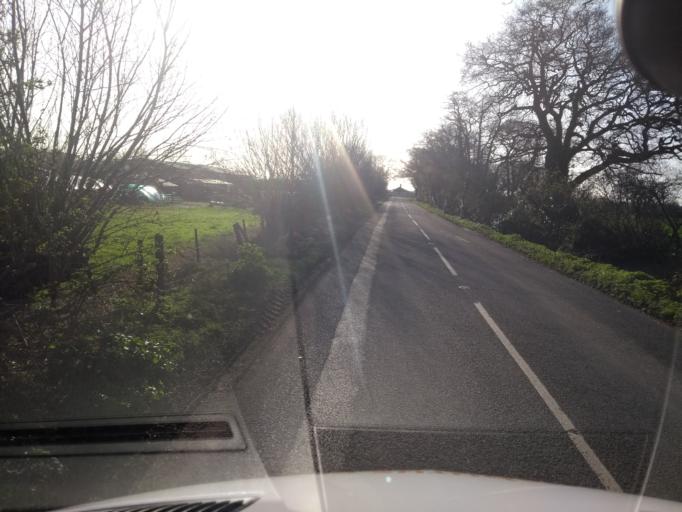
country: GB
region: England
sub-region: Somerset
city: Wedmore
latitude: 51.1869
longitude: -2.8057
